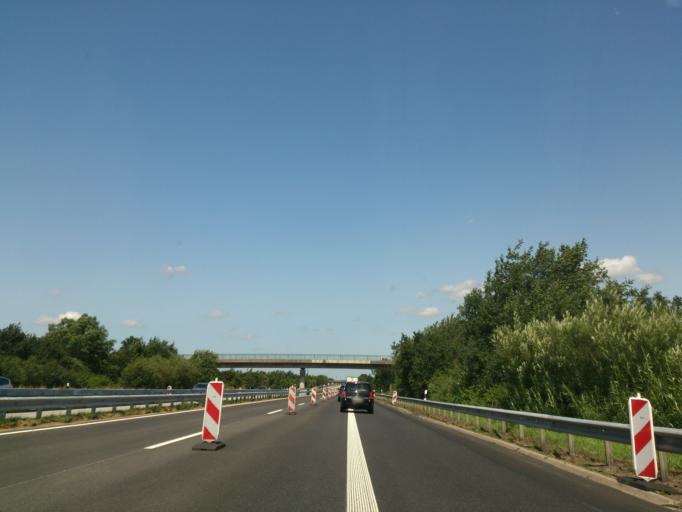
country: DE
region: Schleswig-Holstein
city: Tensbuttel-Rost
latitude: 54.1090
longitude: 9.2629
